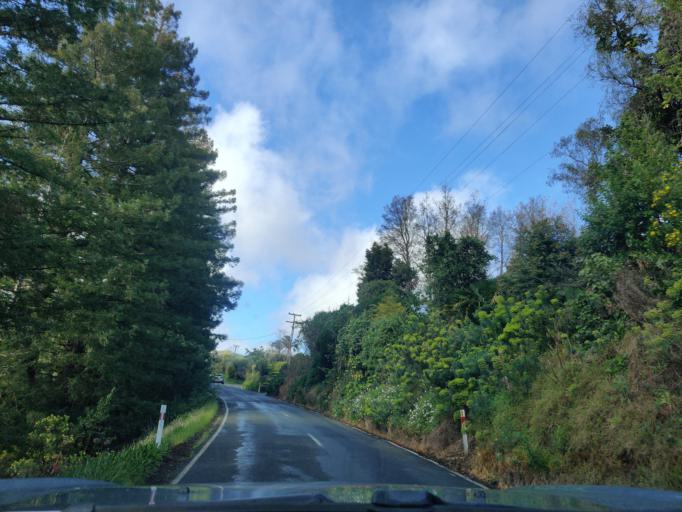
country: NZ
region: Hawke's Bay
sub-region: Hastings District
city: Hastings
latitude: -39.6820
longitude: 176.8974
